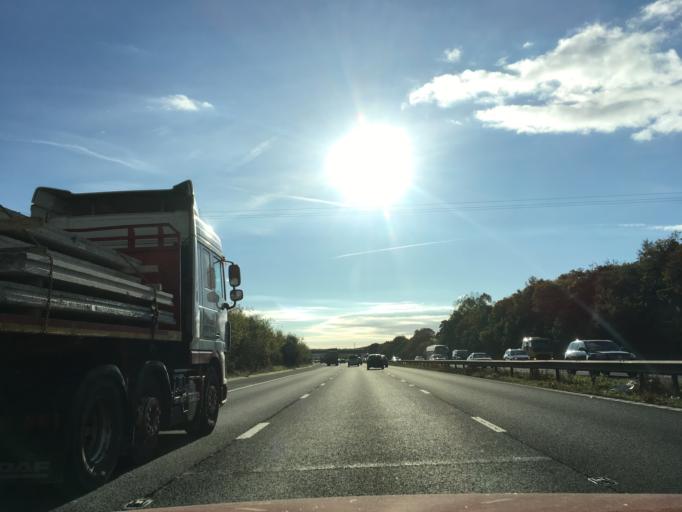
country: GB
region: England
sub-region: South Gloucestershire
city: Alveston
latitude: 51.5755
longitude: -2.5191
